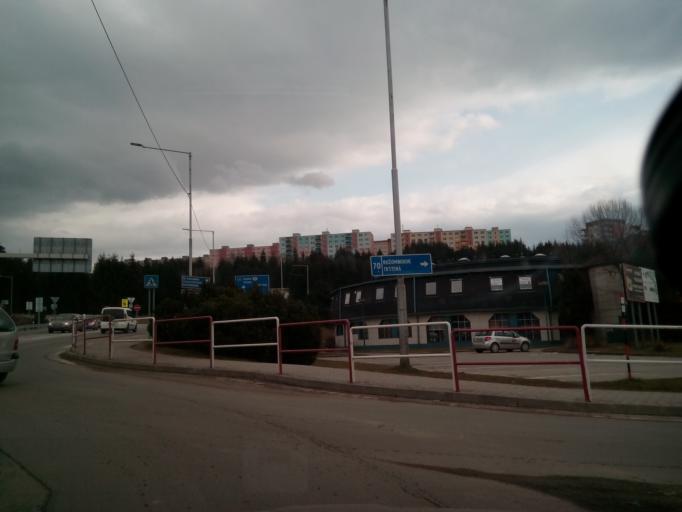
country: SK
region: Zilinsky
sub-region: Okres Dolny Kubin
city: Dolny Kubin
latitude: 49.2125
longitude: 19.2971
